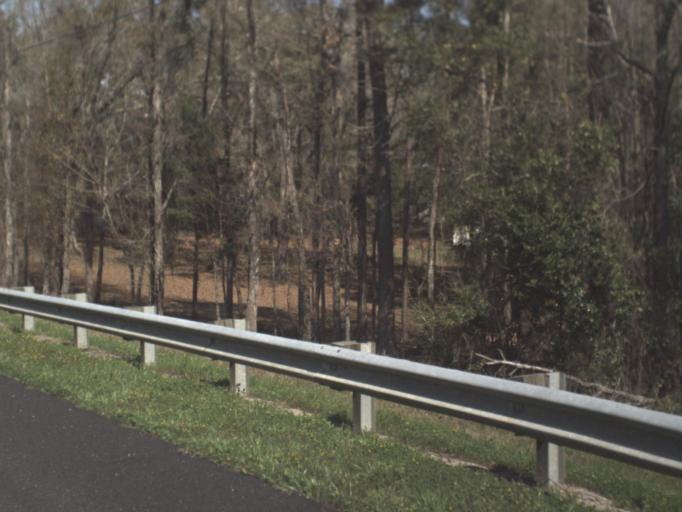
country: US
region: Florida
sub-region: Gadsden County
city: Havana
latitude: 30.5964
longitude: -84.4140
